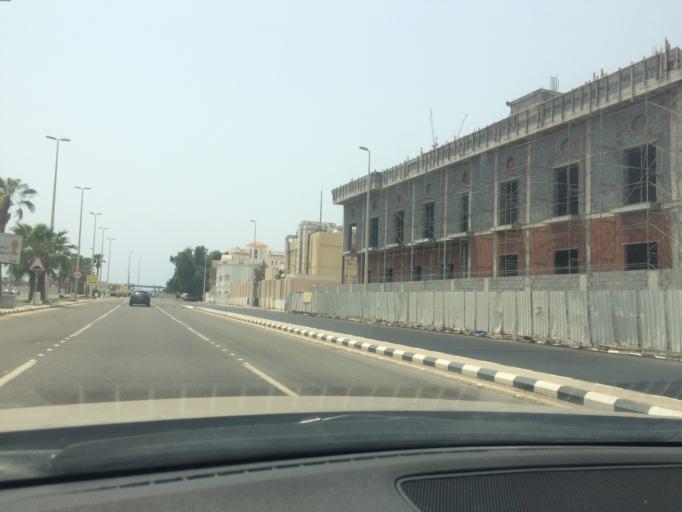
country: SA
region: Makkah
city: Jeddah
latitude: 21.5909
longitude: 39.1135
